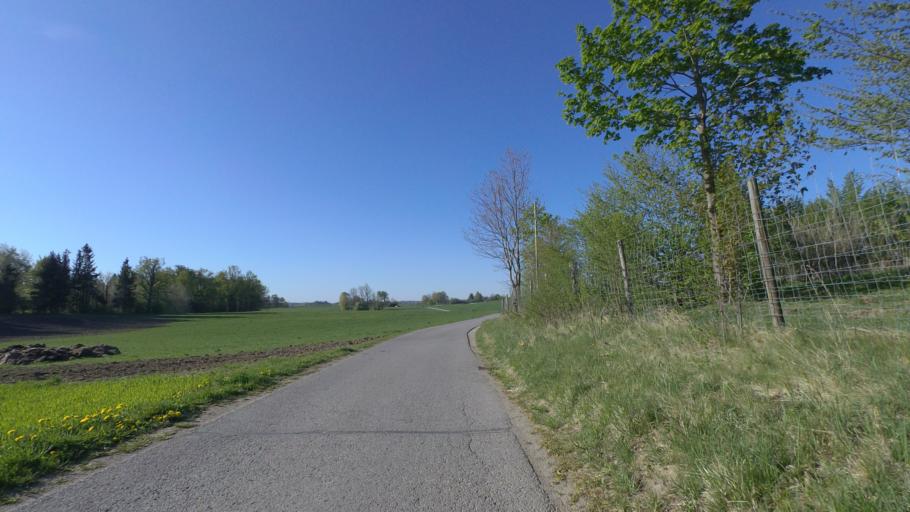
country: DE
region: Bavaria
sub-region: Upper Bavaria
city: Chieming
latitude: 47.8788
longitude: 12.5395
